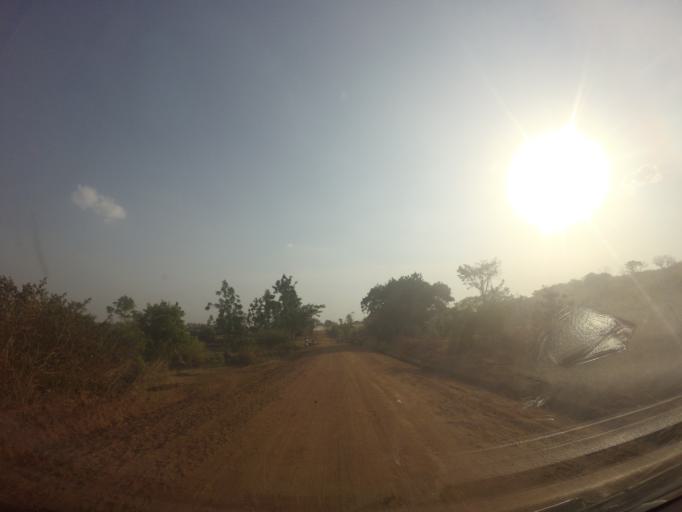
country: UG
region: Northern Region
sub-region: Arua District
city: Arua
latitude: 3.0782
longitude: 31.0858
